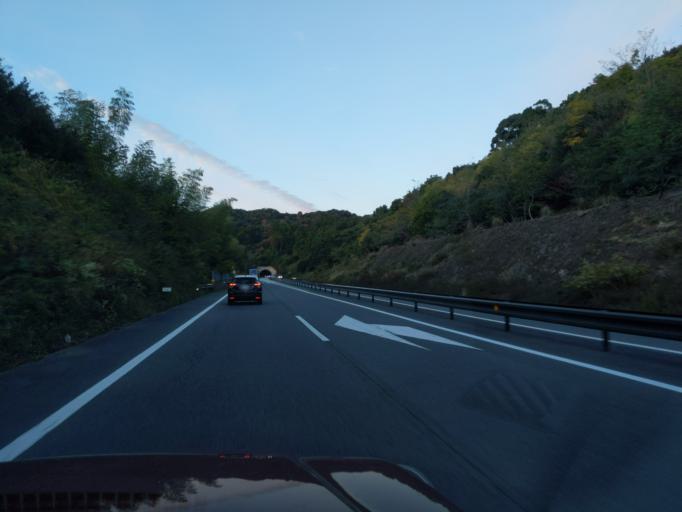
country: JP
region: Tokushima
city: Anan
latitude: 33.7734
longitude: 134.5796
